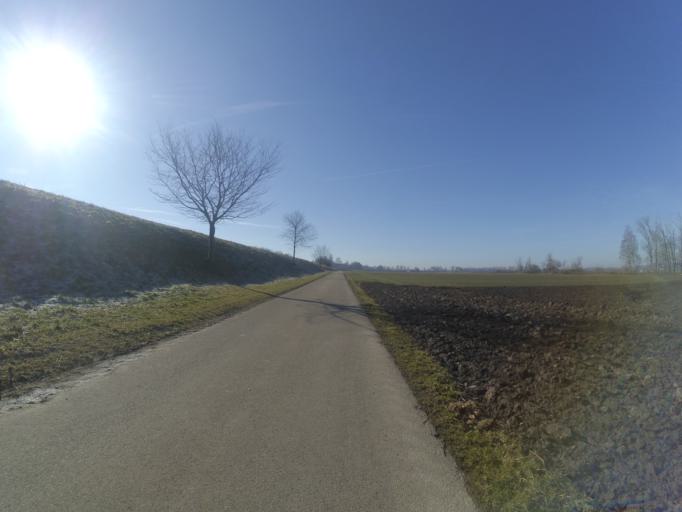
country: DE
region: Baden-Wuerttemberg
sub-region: Tuebingen Region
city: Erbach
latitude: 48.3195
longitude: 9.9188
